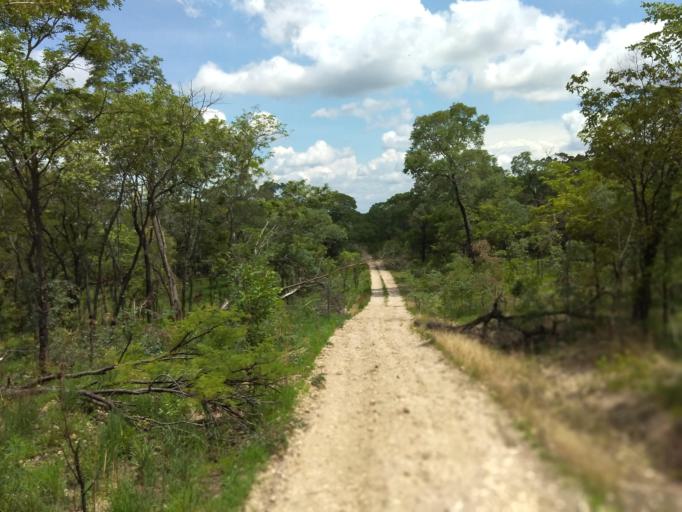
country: ZM
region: Central
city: Mkushi
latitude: -14.0811
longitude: 29.9723
